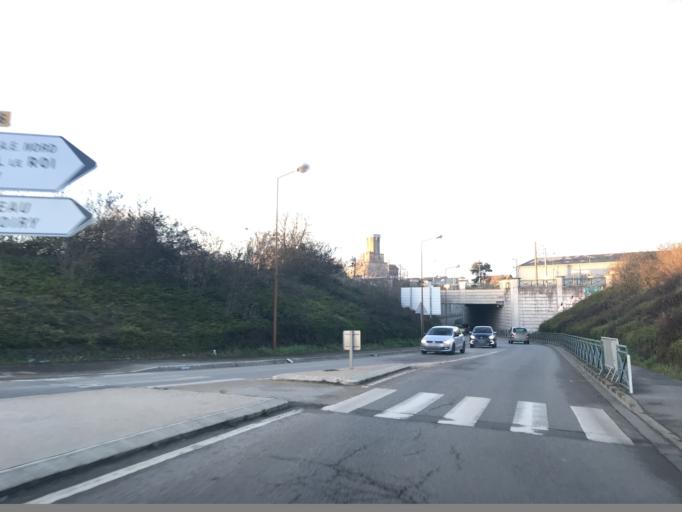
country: FR
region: Ile-de-France
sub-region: Departement des Yvelines
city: Mere
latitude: 48.8017
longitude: 1.8167
